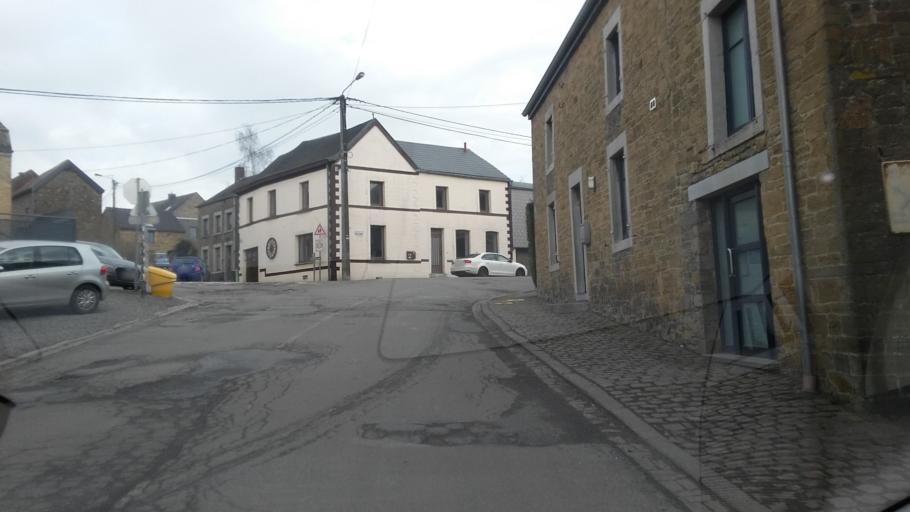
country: BE
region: Wallonia
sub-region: Province de Namur
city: Profondeville
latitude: 50.3783
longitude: 4.8991
